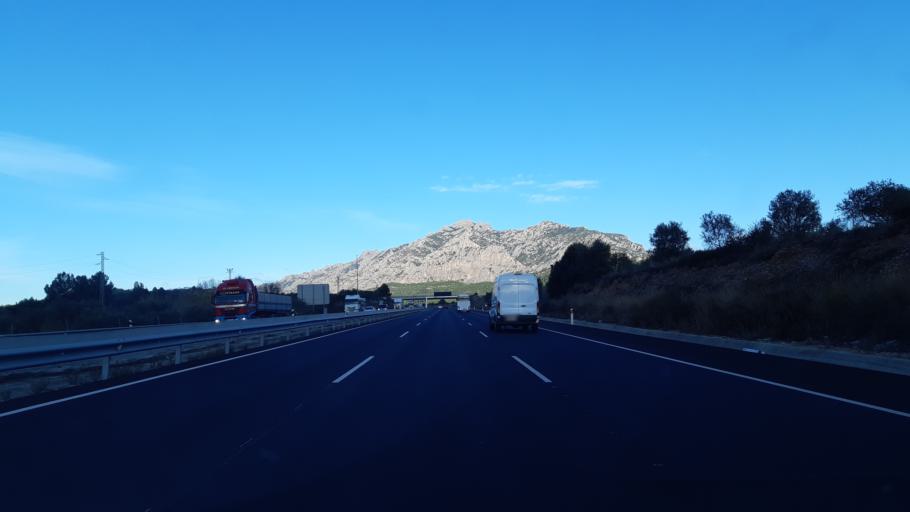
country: ES
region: Catalonia
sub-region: Provincia de Barcelona
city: Esparreguera
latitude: 41.5412
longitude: 1.8569
